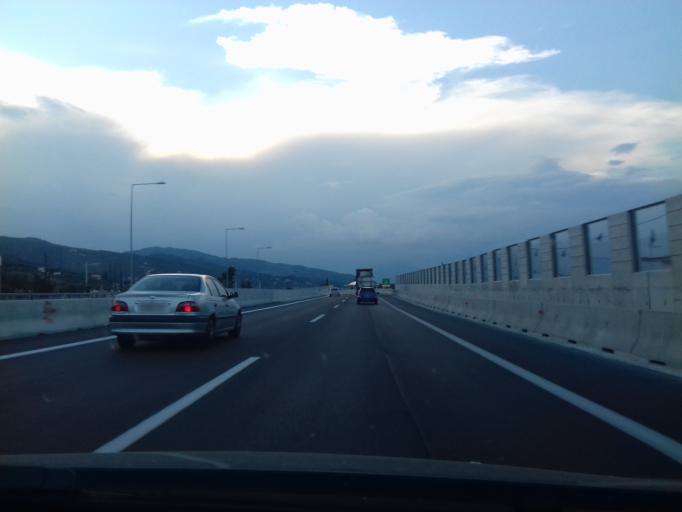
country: GR
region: West Greece
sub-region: Nomos Achaias
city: Selianitika
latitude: 38.2672
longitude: 22.0525
